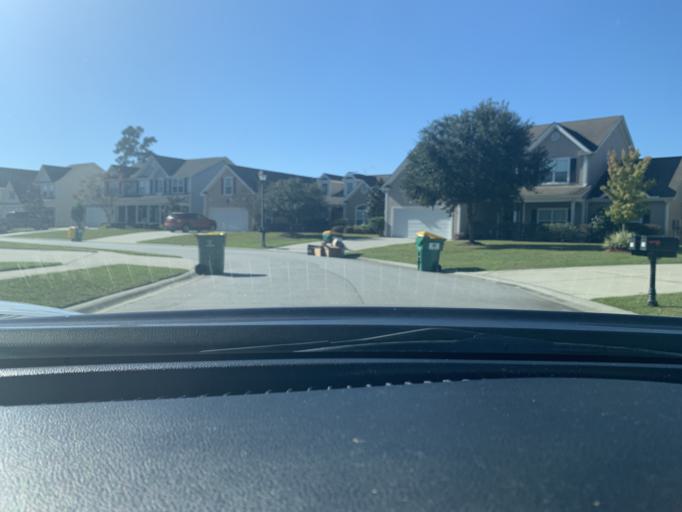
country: US
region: Georgia
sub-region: Chatham County
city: Pooler
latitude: 32.0751
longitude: -81.2691
